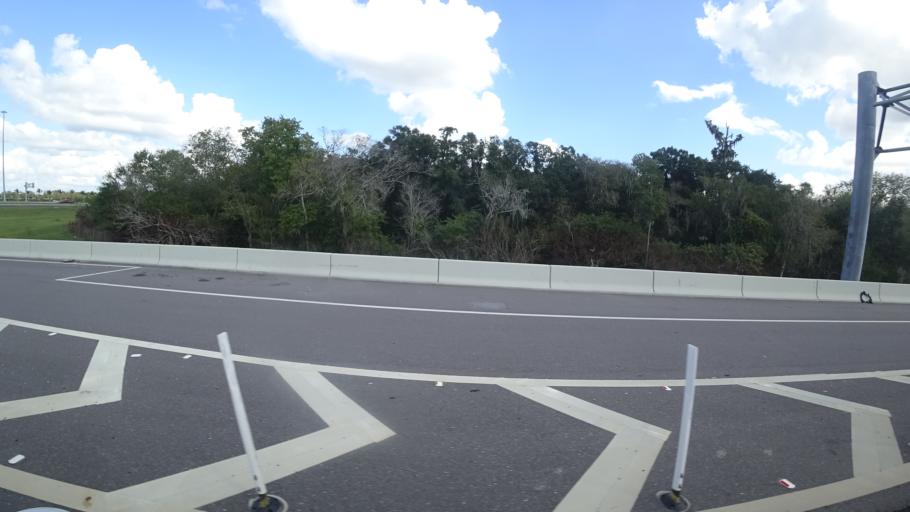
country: US
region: Florida
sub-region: Manatee County
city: Ellenton
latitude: 27.4897
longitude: -82.4704
